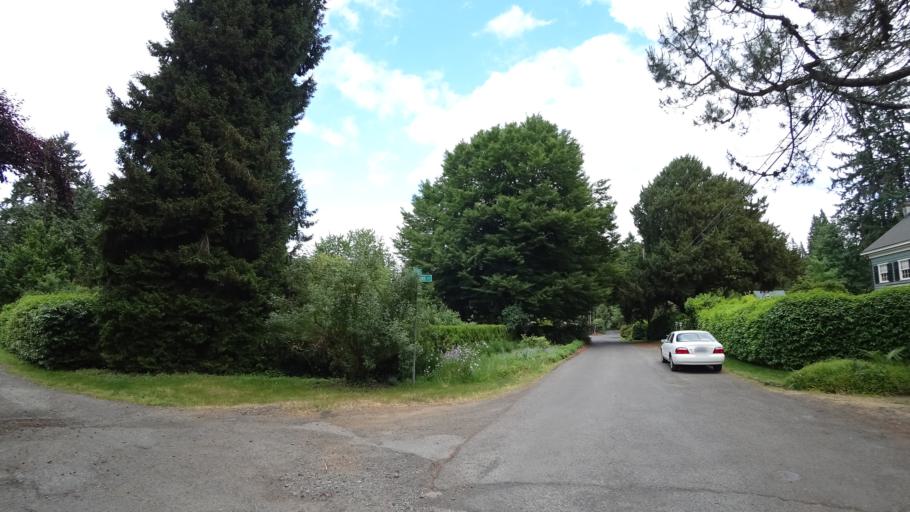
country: US
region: Oregon
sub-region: Clackamas County
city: Milwaukie
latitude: 45.4493
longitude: -122.6619
